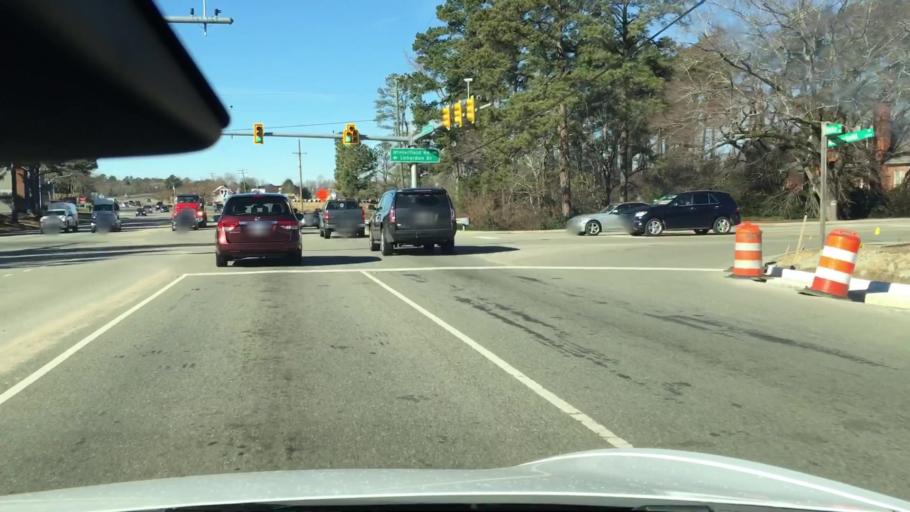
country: US
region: Virginia
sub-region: Chesterfield County
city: Brandermill
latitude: 37.5060
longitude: -77.6619
